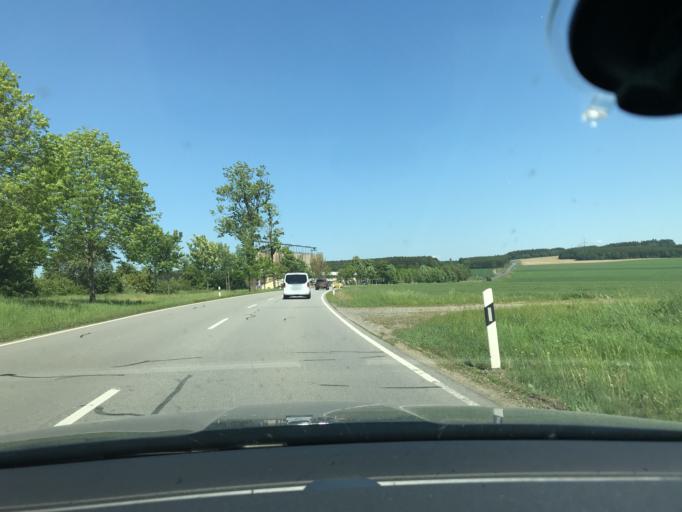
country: DE
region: Saxony
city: Zwonitz
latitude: 50.6537
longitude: 12.8109
